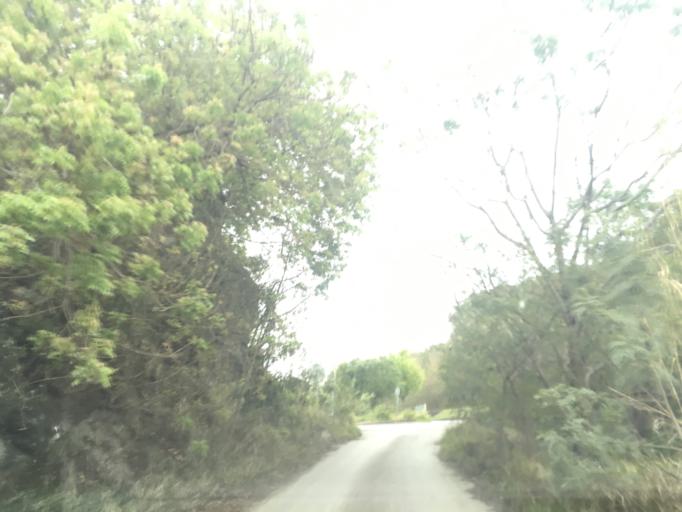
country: TW
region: Taiwan
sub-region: Taitung
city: Taitung
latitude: 22.8100
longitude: 121.1381
